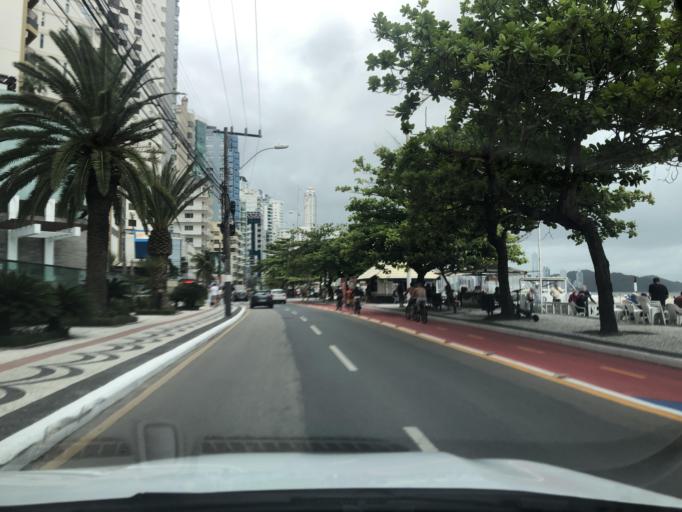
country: BR
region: Santa Catarina
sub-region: Balneario Camboriu
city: Balneario Camboriu
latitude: -26.9987
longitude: -48.6233
